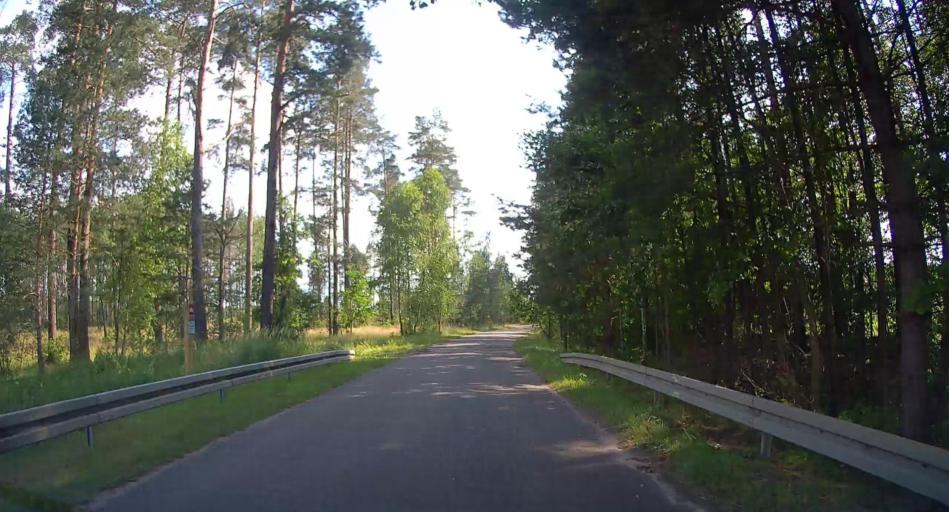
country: PL
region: Masovian Voivodeship
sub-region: Powiat ostrowski
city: Brok
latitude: 52.7399
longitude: 21.7470
